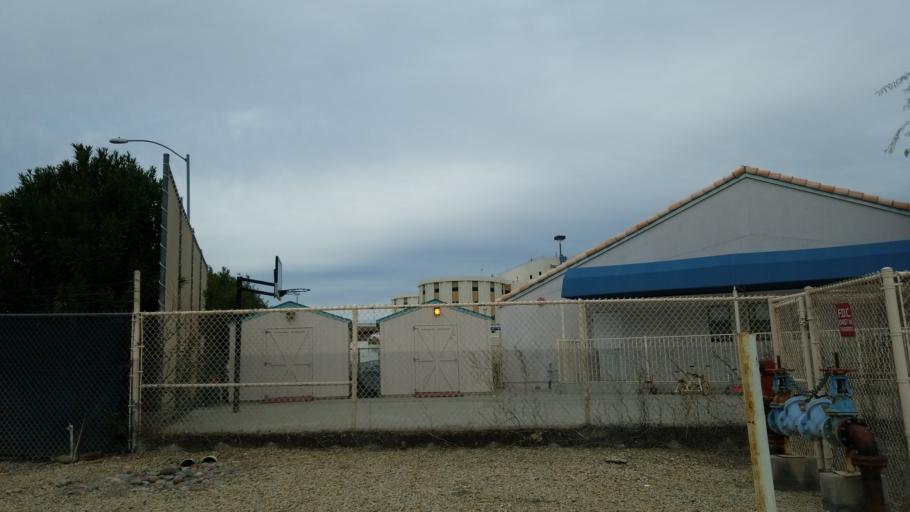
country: US
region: Arizona
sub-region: Maricopa County
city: Sun City
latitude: 33.6019
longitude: -112.2846
